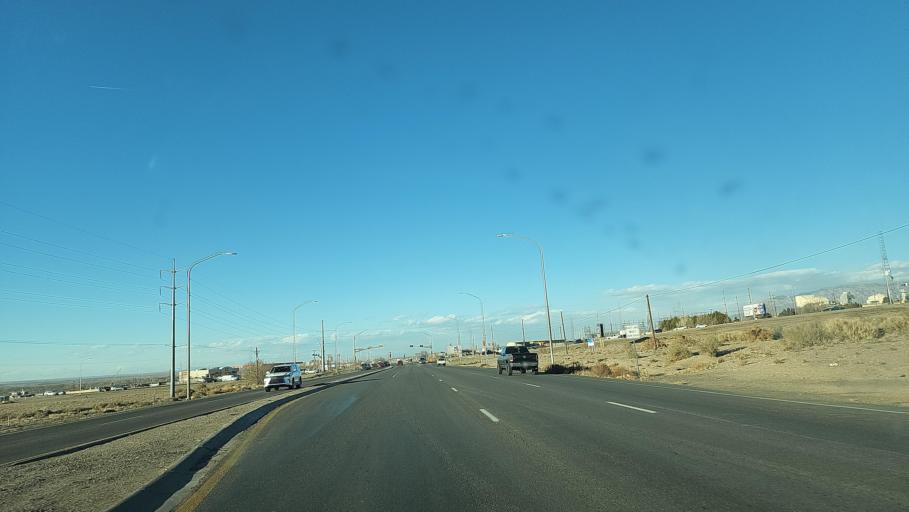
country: US
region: New Mexico
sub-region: Bernalillo County
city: South Valley
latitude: 35.0231
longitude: -106.6467
